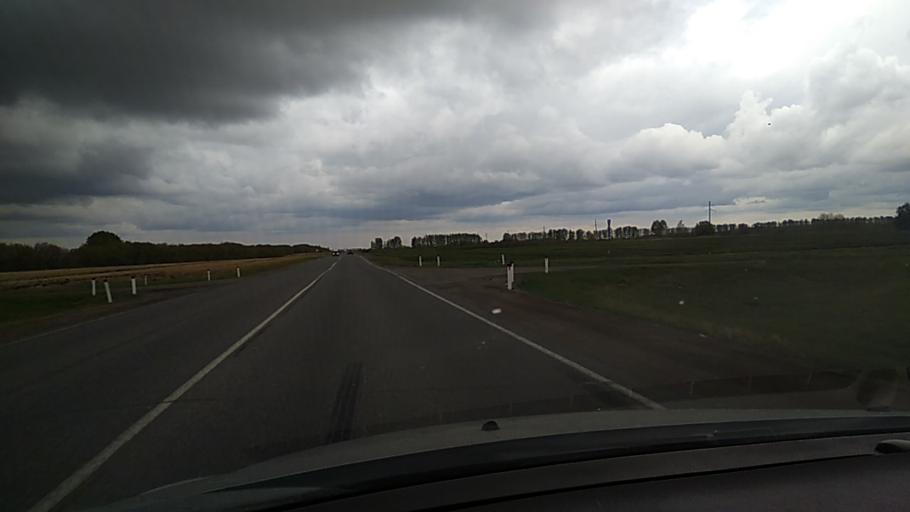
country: RU
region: Kurgan
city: Dalmatovo
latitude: 56.2898
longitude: 62.8387
